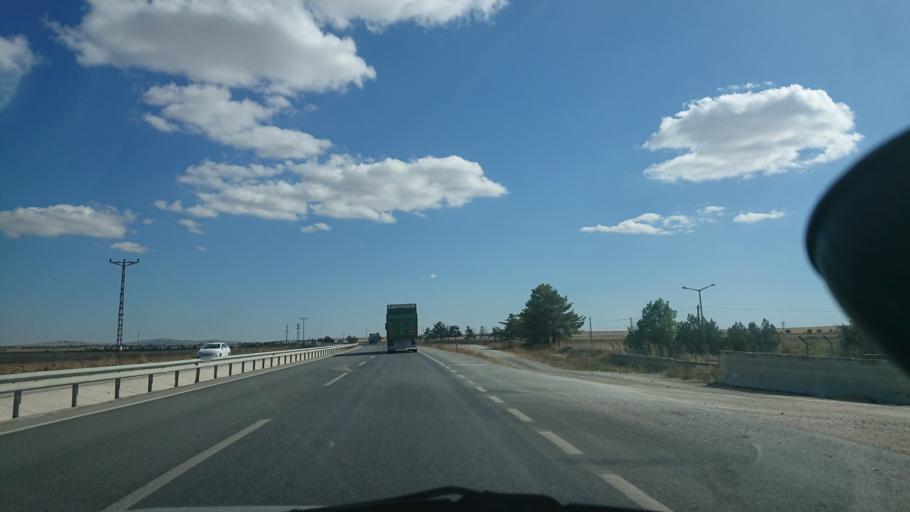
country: TR
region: Eskisehir
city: Mahmudiye
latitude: 39.5611
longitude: 30.9164
